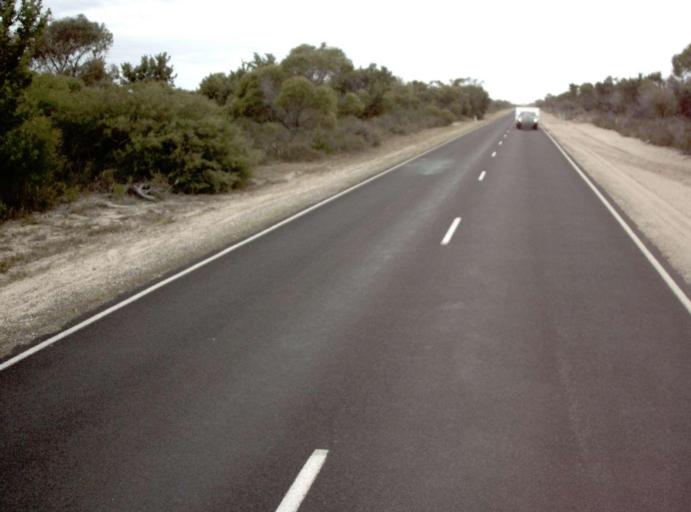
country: AU
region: Victoria
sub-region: East Gippsland
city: Bairnsdale
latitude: -38.1148
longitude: 147.4637
